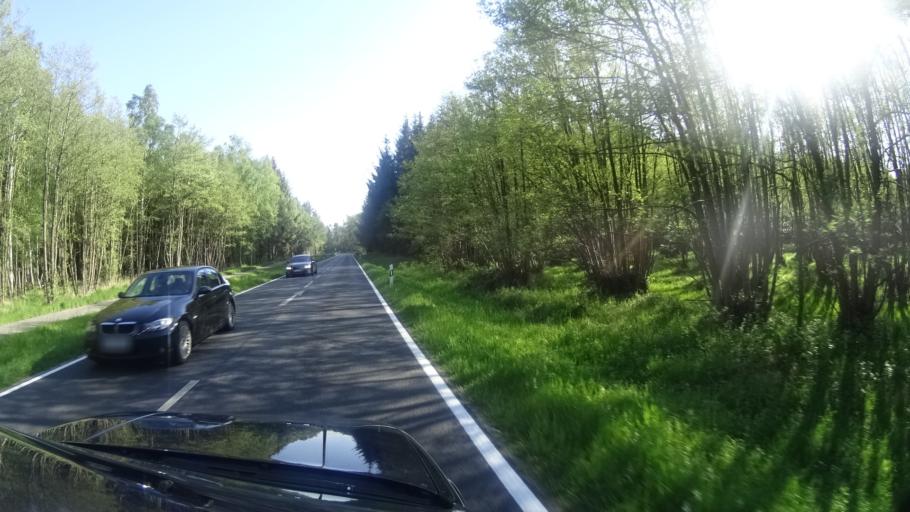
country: DE
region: Mecklenburg-Vorpommern
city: Ostseebad Prerow
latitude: 54.4264
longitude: 12.5727
